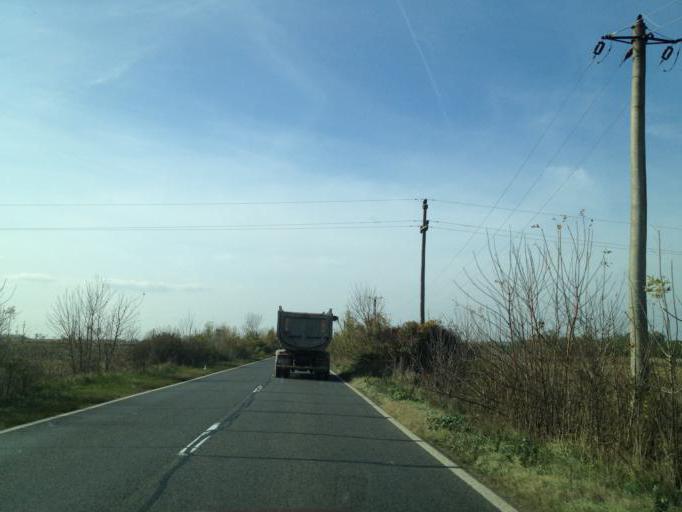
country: RO
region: Timis
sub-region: Comuna Faget
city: Faget
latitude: 45.8586
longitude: 22.2094
